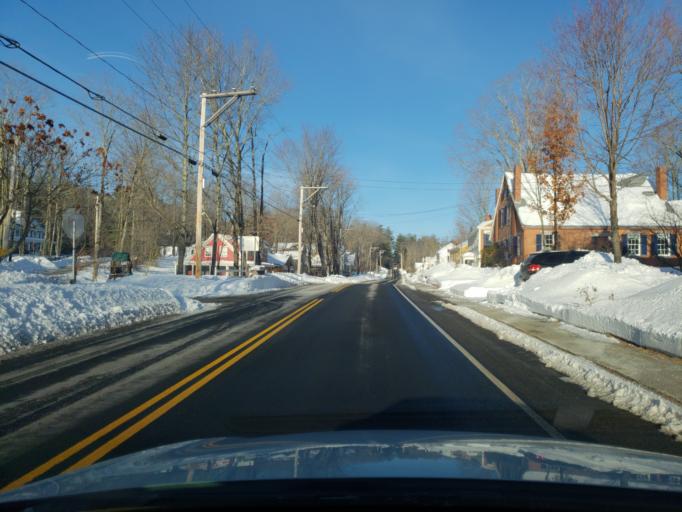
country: US
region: New Hampshire
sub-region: Hillsborough County
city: Greenfield
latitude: 42.9903
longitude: -71.8152
